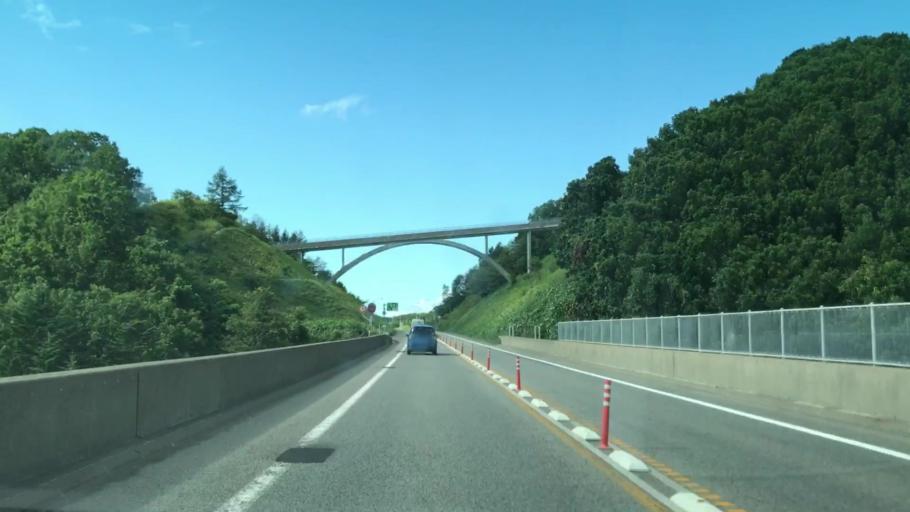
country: JP
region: Hokkaido
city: Date
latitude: 42.4602
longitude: 140.9114
